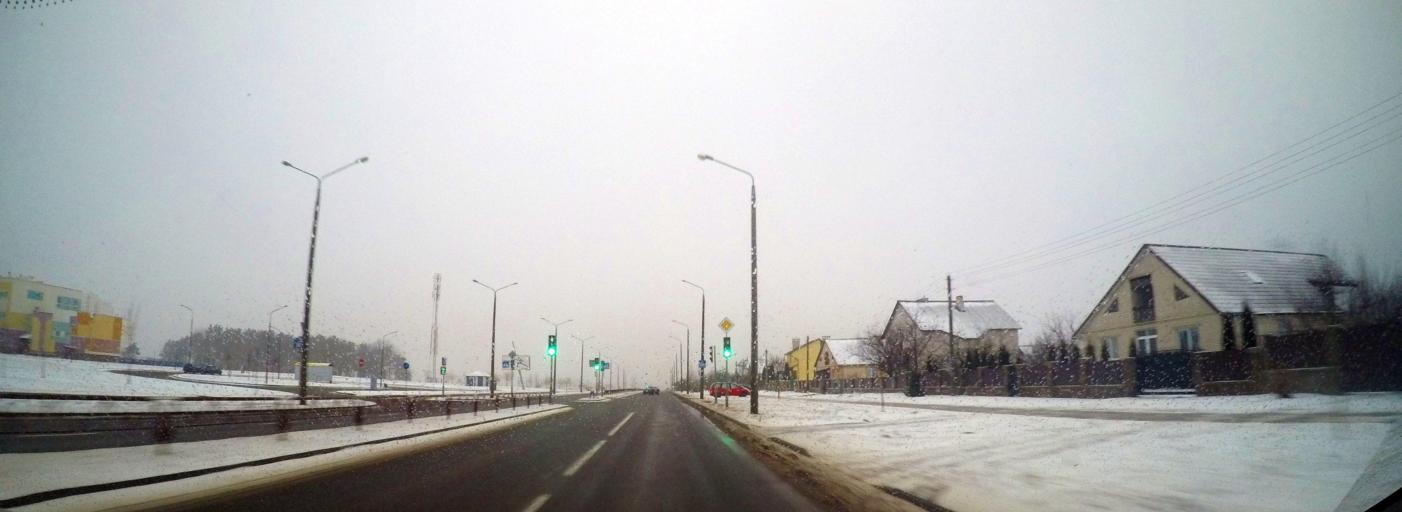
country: BY
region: Grodnenskaya
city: Hrodna
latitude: 53.6256
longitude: 23.8089
